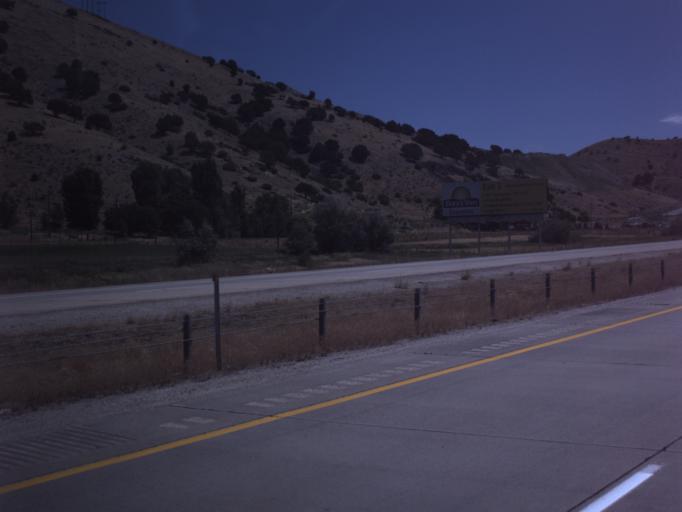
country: US
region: Utah
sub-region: Morgan County
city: Morgan
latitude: 41.0440
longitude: -111.6691
